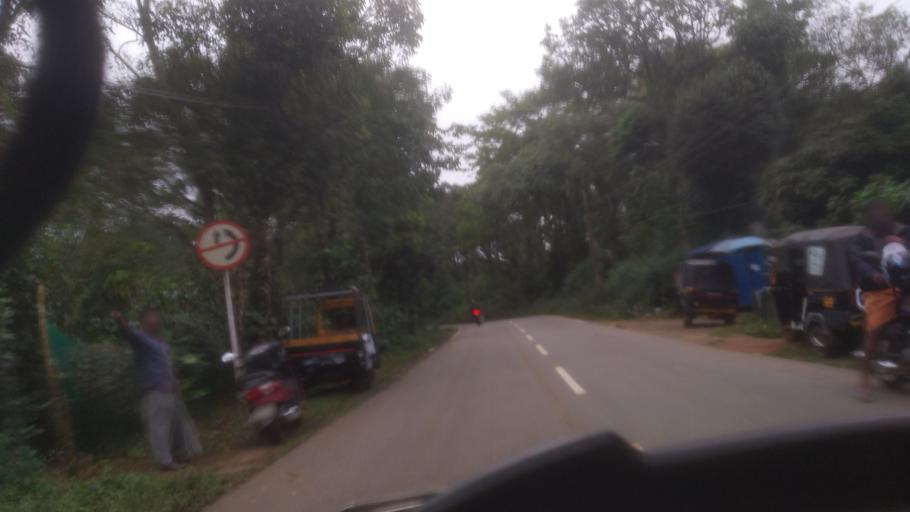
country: IN
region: Tamil Nadu
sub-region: Theni
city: Kombai
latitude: 9.8949
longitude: 77.1969
